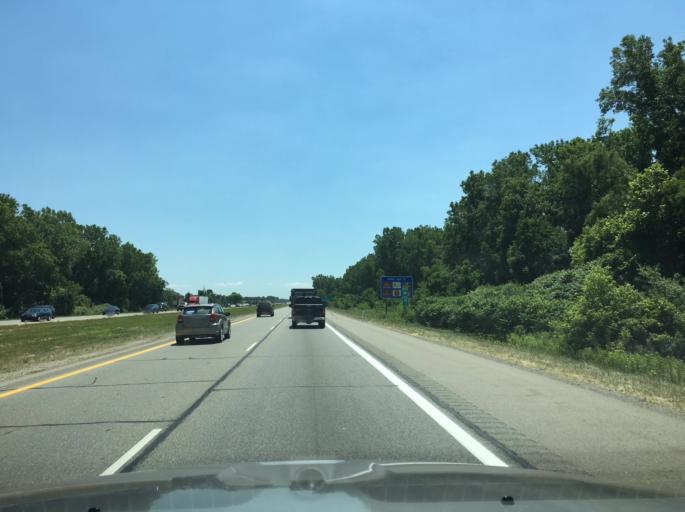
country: US
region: Michigan
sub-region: Macomb County
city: Utica
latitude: 42.6357
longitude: -83.0137
